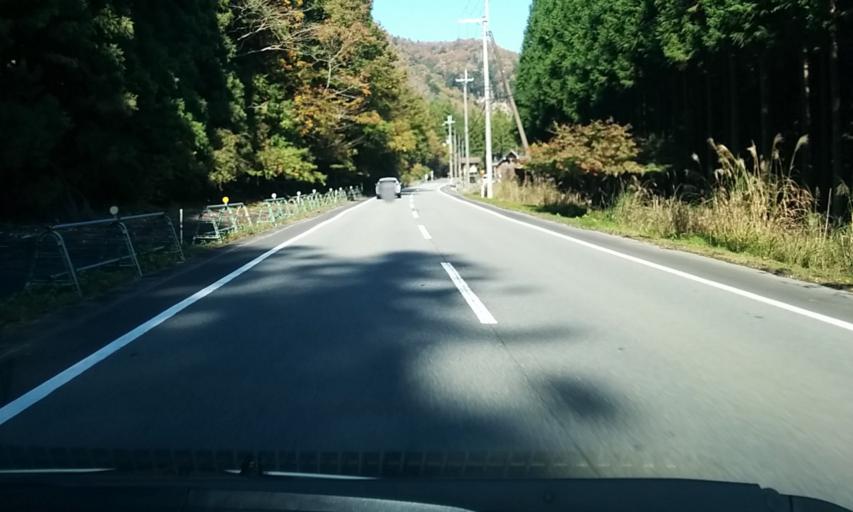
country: JP
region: Kyoto
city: Kameoka
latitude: 35.2155
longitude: 135.5692
